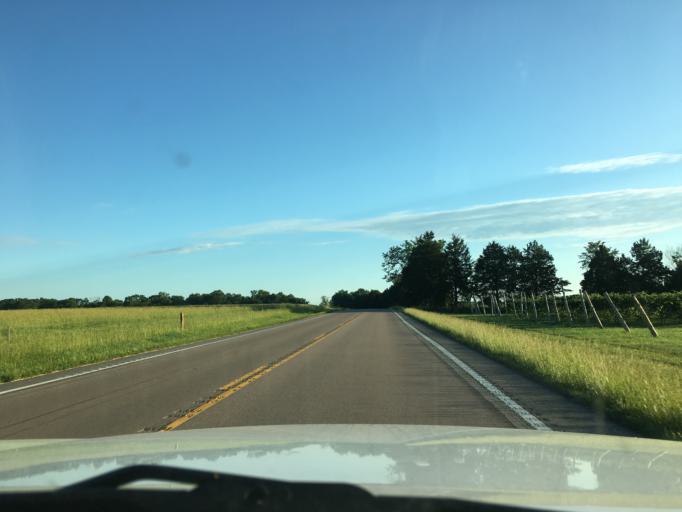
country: US
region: Missouri
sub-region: Gasconade County
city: Owensville
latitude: 38.4468
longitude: -91.4467
